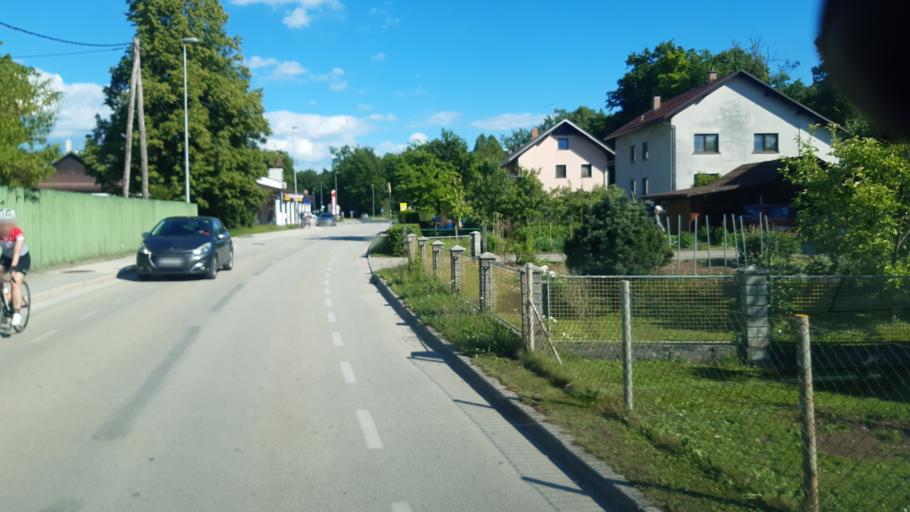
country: SI
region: Sencur
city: Hrastje
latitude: 46.2166
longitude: 14.3738
